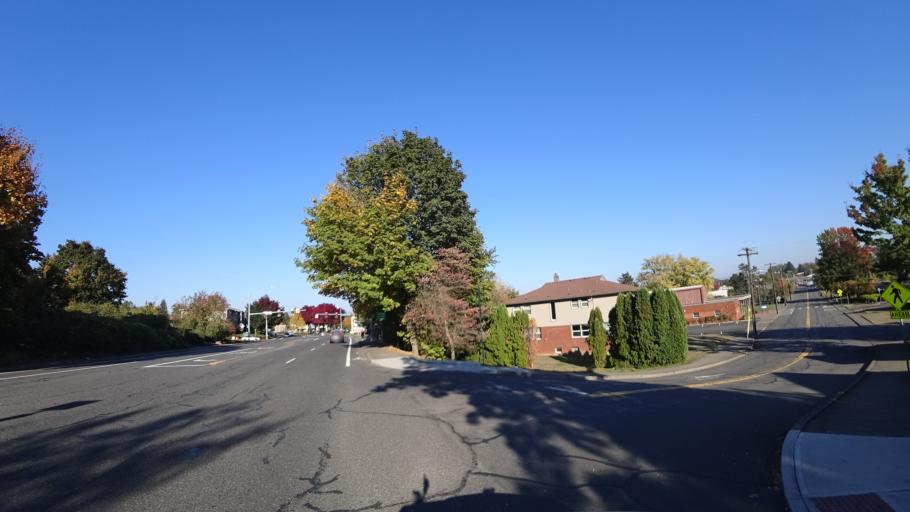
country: US
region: Oregon
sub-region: Multnomah County
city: Gresham
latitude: 45.4987
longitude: -122.4375
